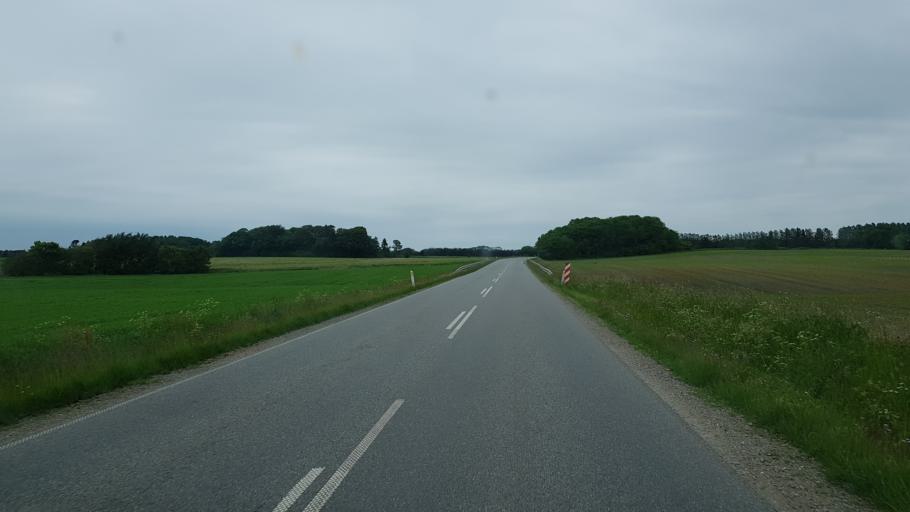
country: DK
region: South Denmark
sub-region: Varde Kommune
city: Olgod
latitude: 55.7129
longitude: 8.6983
